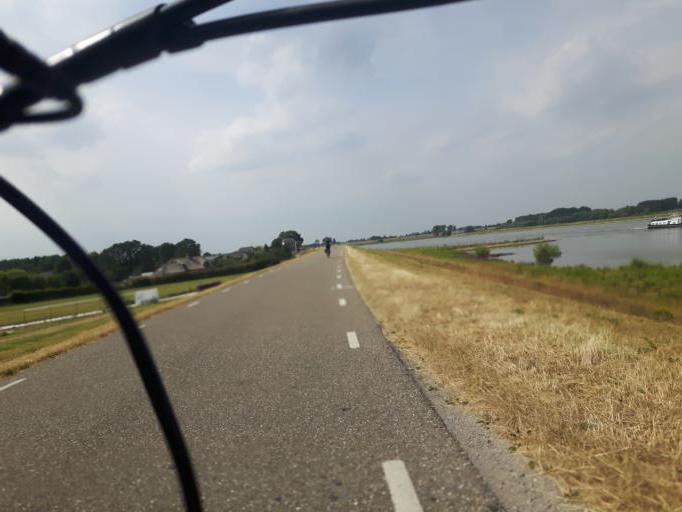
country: NL
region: Gelderland
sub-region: Gemeente Zaltbommel
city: Nederhemert
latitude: 51.8105
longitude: 5.1875
